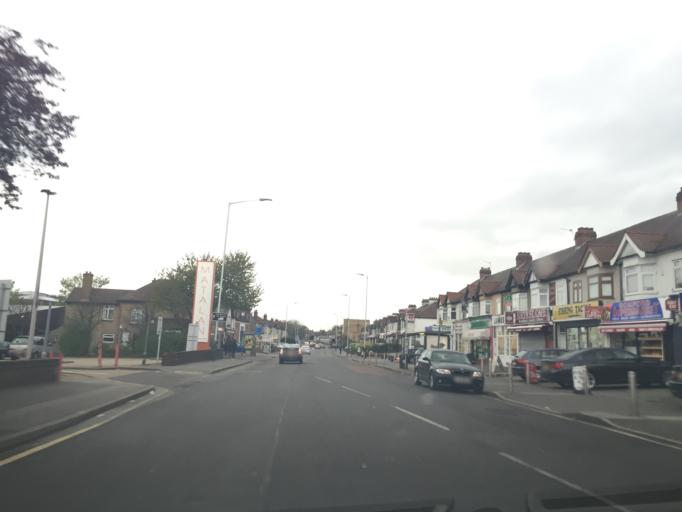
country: GB
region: England
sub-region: Greater London
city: Romford
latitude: 51.5815
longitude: 0.1771
